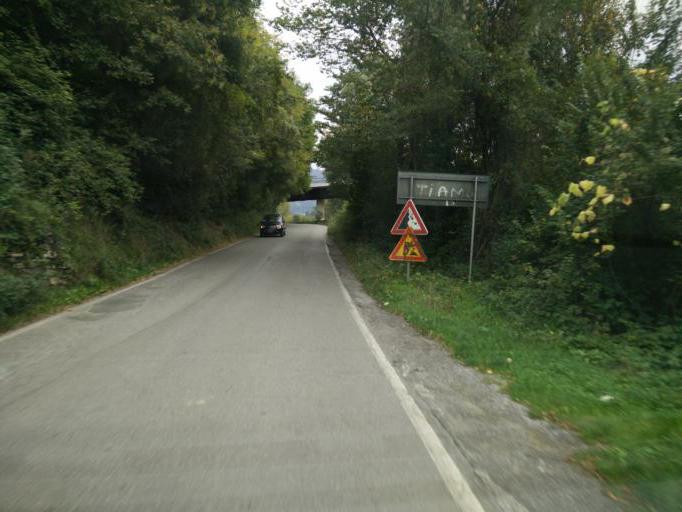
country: IT
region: Tuscany
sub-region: Provincia di Massa-Carrara
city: Fivizzano
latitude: 44.2004
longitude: 10.1052
